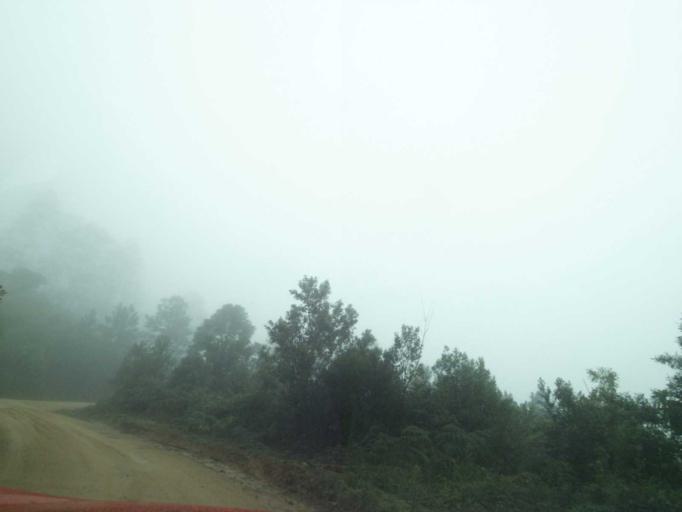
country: BR
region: Santa Catarina
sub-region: Anitapolis
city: Anitapolis
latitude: -27.9153
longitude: -49.1741
